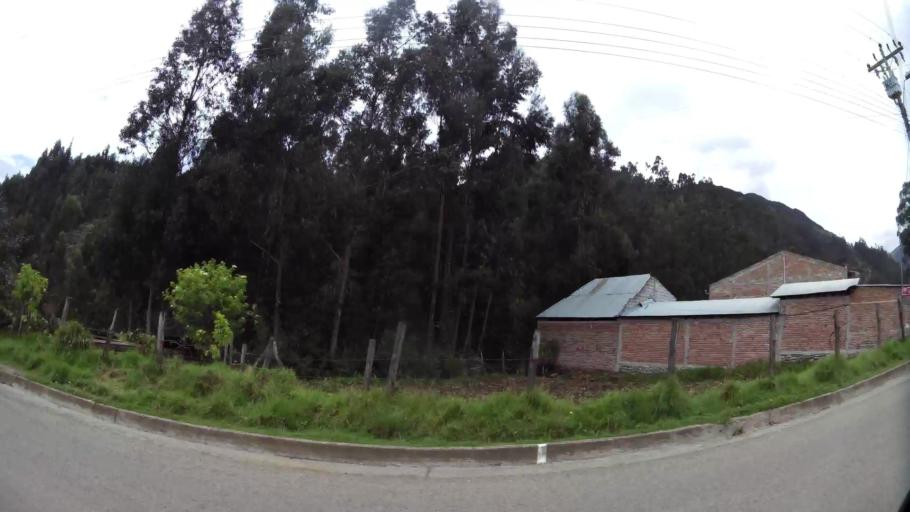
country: EC
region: Azuay
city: Cuenca
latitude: -2.8740
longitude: -79.0751
